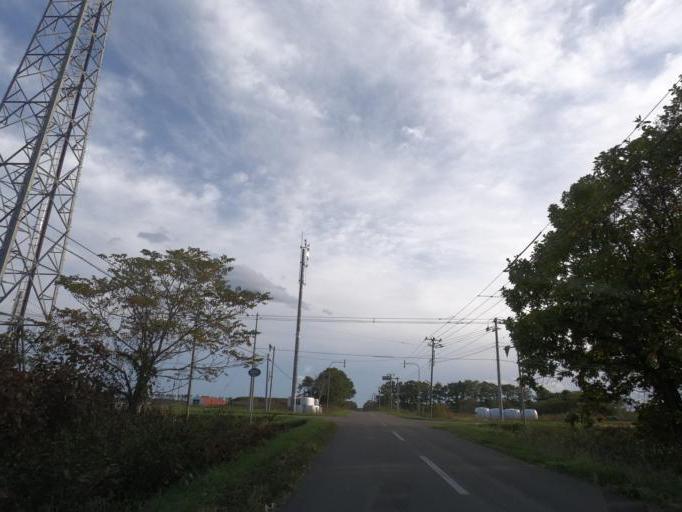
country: JP
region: Hokkaido
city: Obihiro
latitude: 42.4993
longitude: 143.4177
